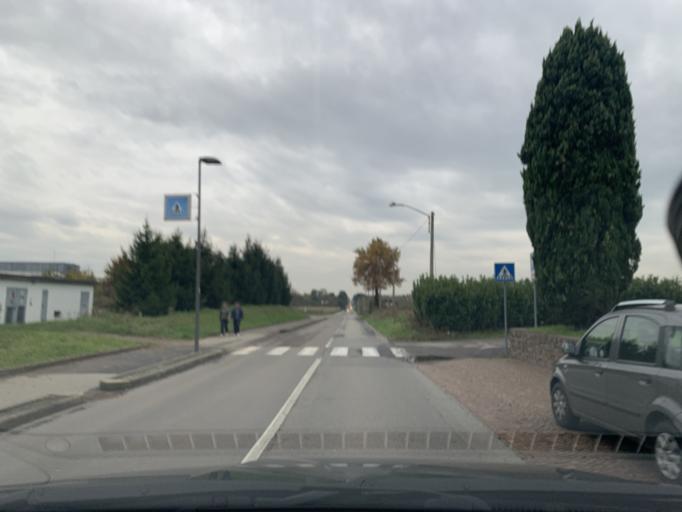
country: IT
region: Lombardy
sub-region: Provincia di Como
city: Puginate
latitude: 45.7086
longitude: 9.0566
